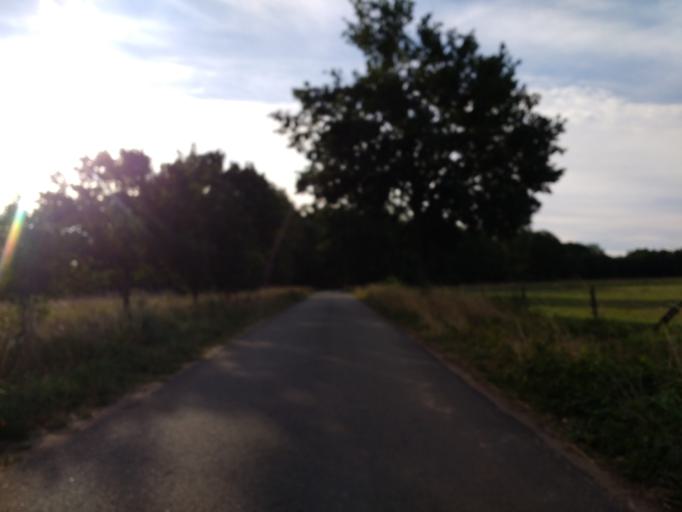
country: DE
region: Lower Saxony
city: Gifhorn
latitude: 52.4498
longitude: 10.5552
